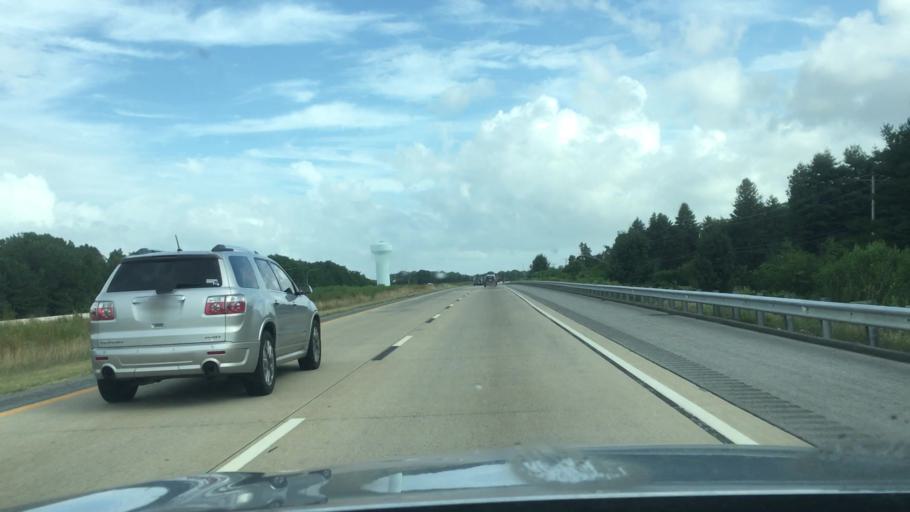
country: US
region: Delaware
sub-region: New Castle County
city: Townsend
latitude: 39.4317
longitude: -75.6600
